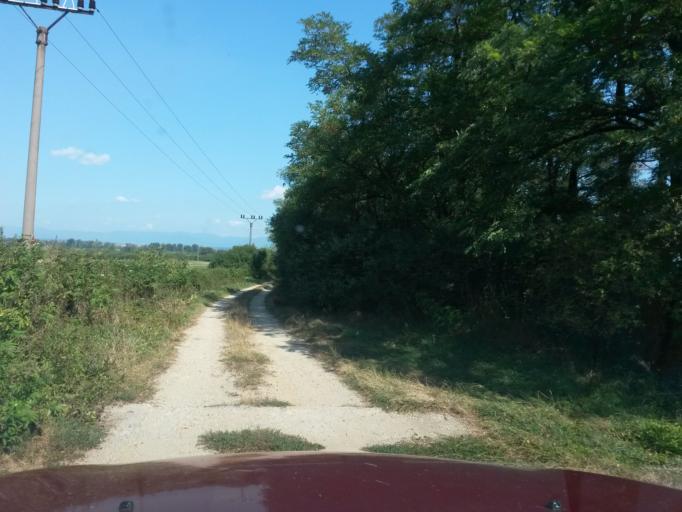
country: HU
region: Borsod-Abauj-Zemplen
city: Gonc
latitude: 48.5334
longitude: 21.1577
